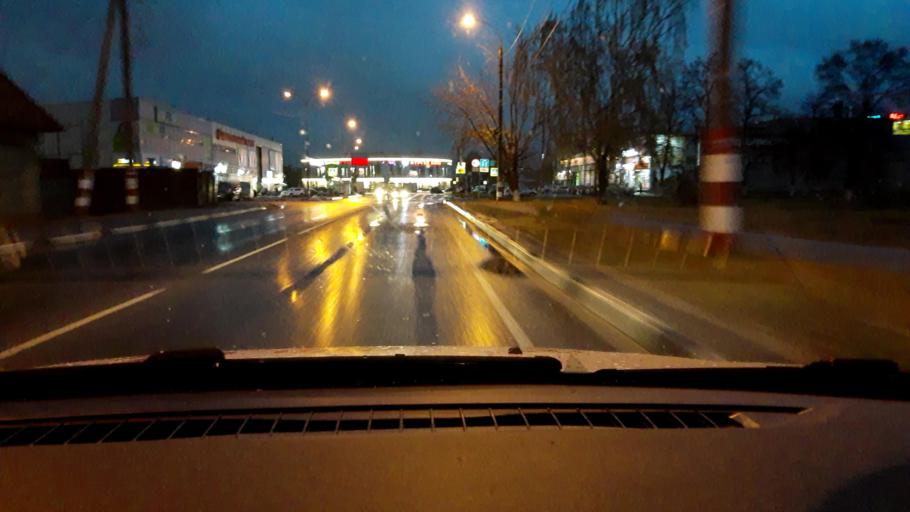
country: RU
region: Nizjnij Novgorod
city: Bor
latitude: 56.3610
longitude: 44.0509
